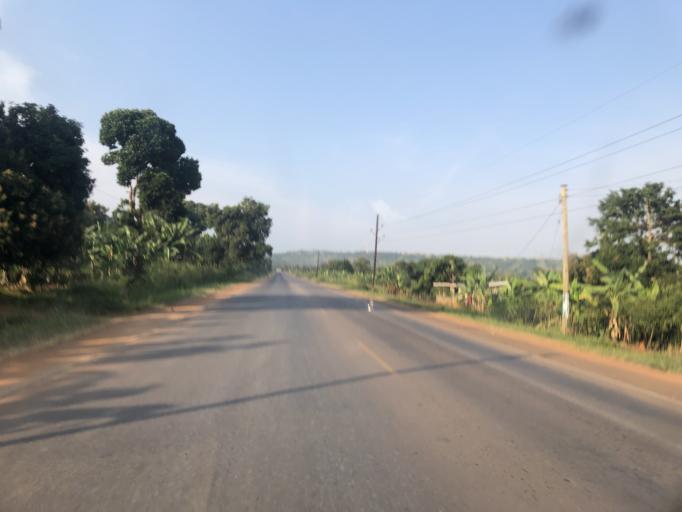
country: UG
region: Central Region
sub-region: Mpigi District
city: Mpigi
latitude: 0.1325
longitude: 32.2097
